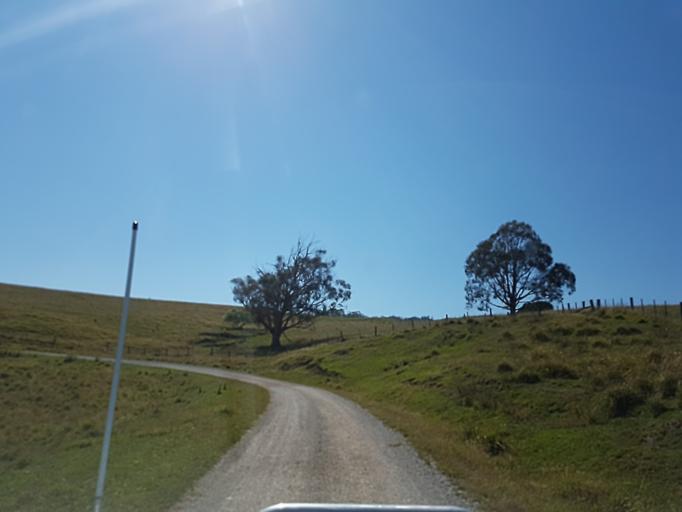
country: AU
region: Victoria
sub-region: East Gippsland
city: Lakes Entrance
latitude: -37.2346
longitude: 148.2689
